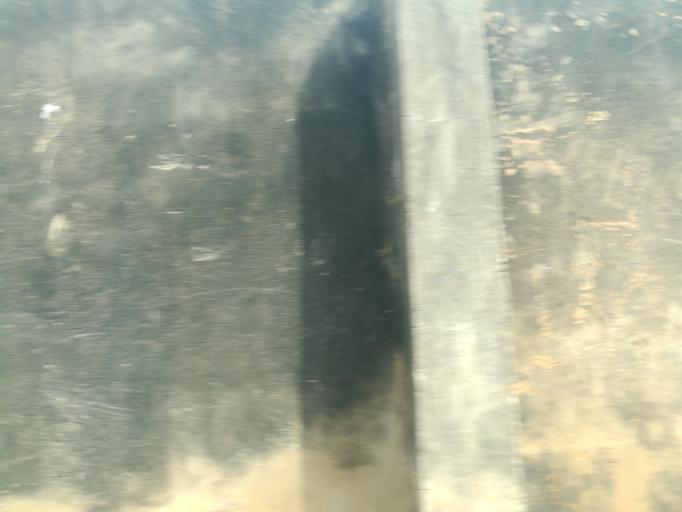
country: NG
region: Oyo
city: Ibadan
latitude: 7.4141
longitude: 3.9536
